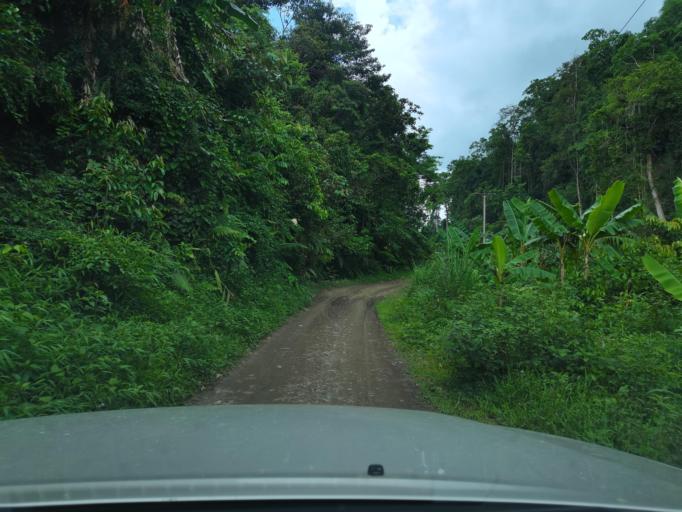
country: LA
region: Loungnamtha
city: Muang Long
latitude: 20.7774
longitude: 101.0168
